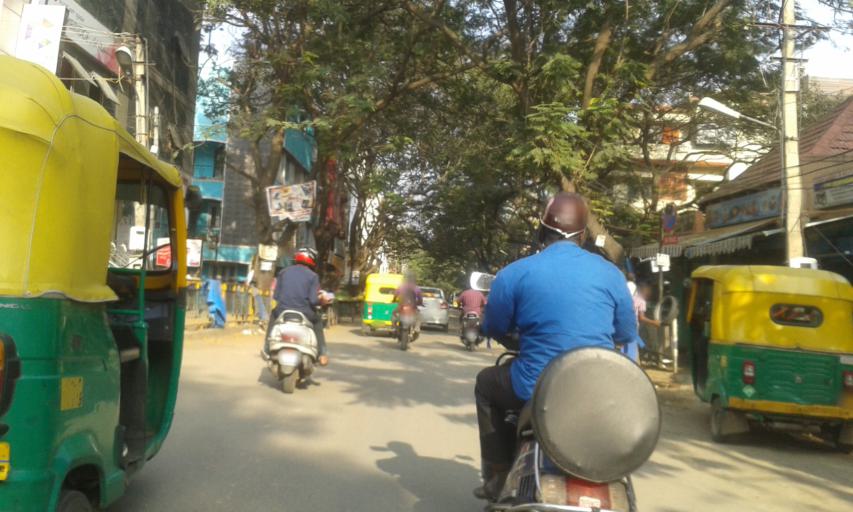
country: IN
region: Karnataka
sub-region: Bangalore Urban
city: Bangalore
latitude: 12.9697
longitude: 77.6305
